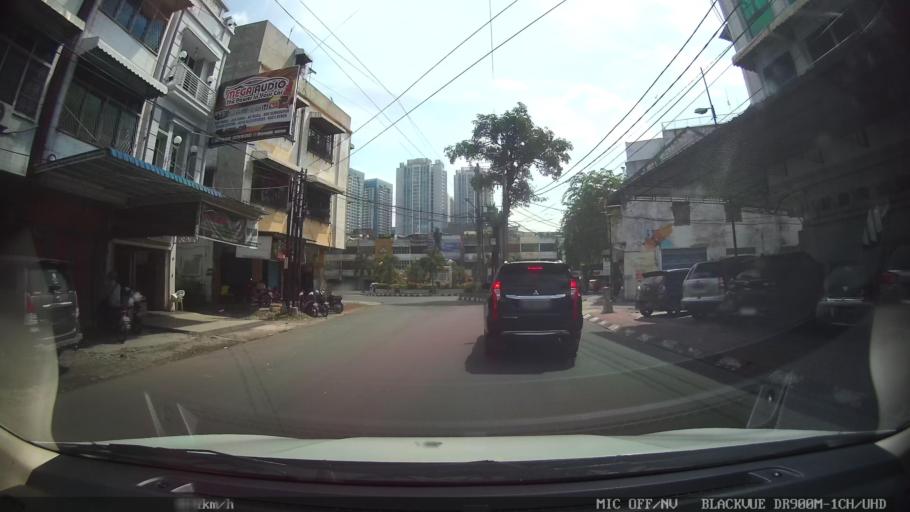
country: ID
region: North Sumatra
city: Medan
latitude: 3.5910
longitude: 98.6705
